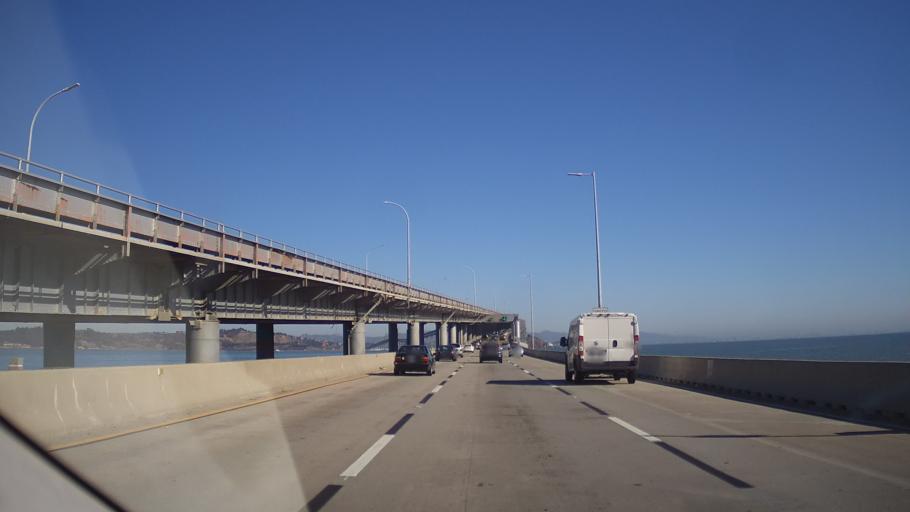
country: US
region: California
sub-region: Marin County
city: Strawberry
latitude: 37.9410
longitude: -122.4670
